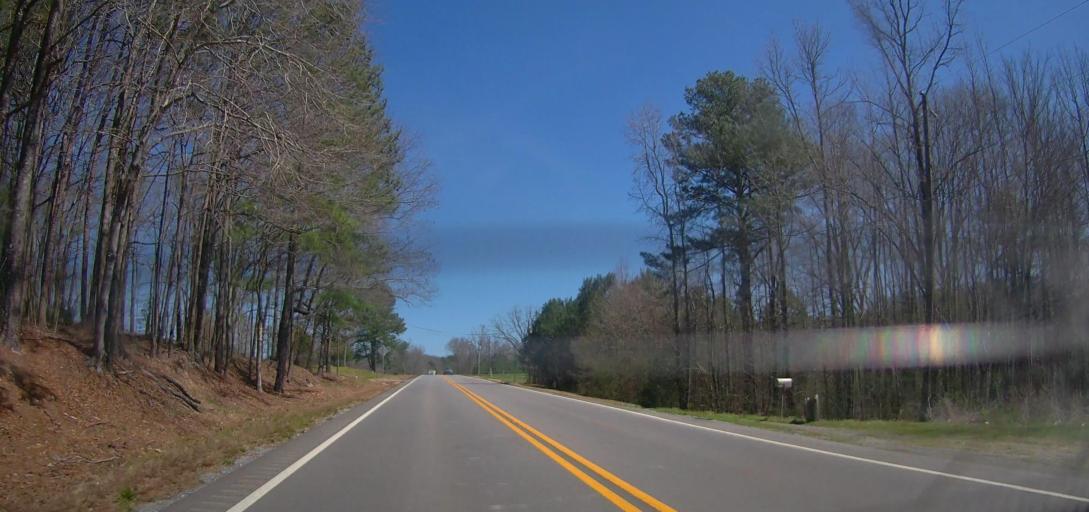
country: US
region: Alabama
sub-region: Saint Clair County
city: Steele
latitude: 34.0667
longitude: -86.2717
